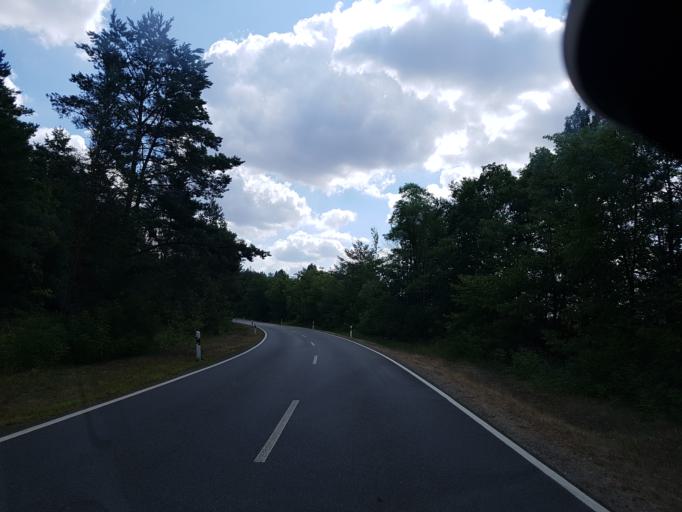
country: DE
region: Brandenburg
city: Drebkau
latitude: 51.6792
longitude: 14.1561
